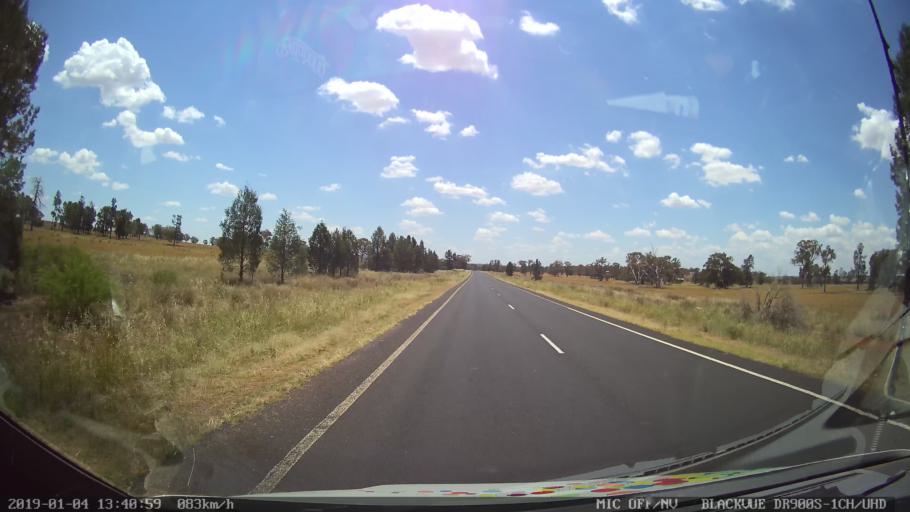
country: AU
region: New South Wales
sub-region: Dubbo Municipality
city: Dubbo
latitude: -32.5081
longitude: 148.5540
